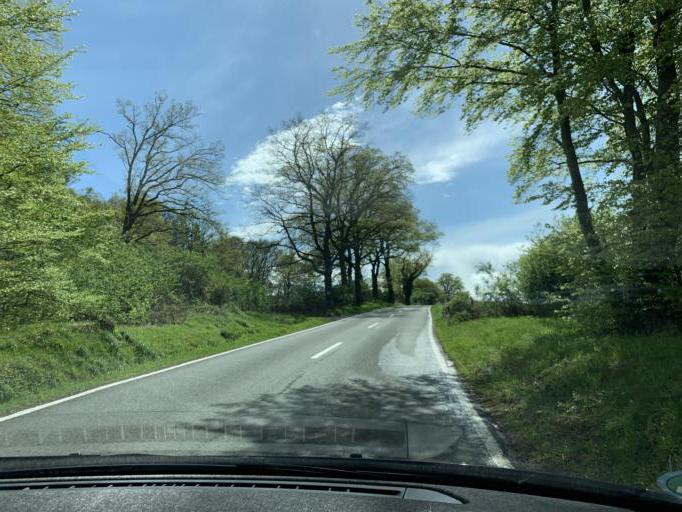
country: DE
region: North Rhine-Westphalia
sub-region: Regierungsbezirk Koln
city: Bad Munstereifel
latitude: 50.5845
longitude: 6.7120
